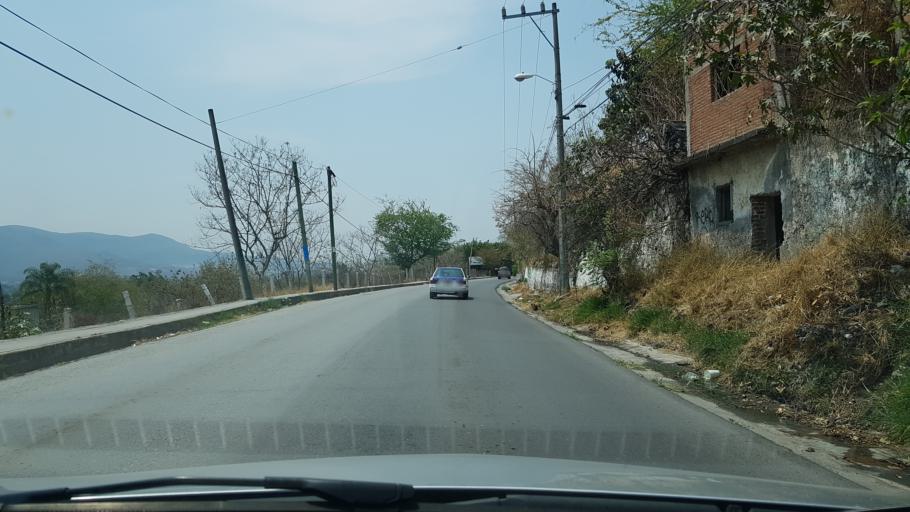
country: MX
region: Morelos
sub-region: Jiutepec
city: Jiutepec
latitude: 18.8728
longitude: -99.1727
